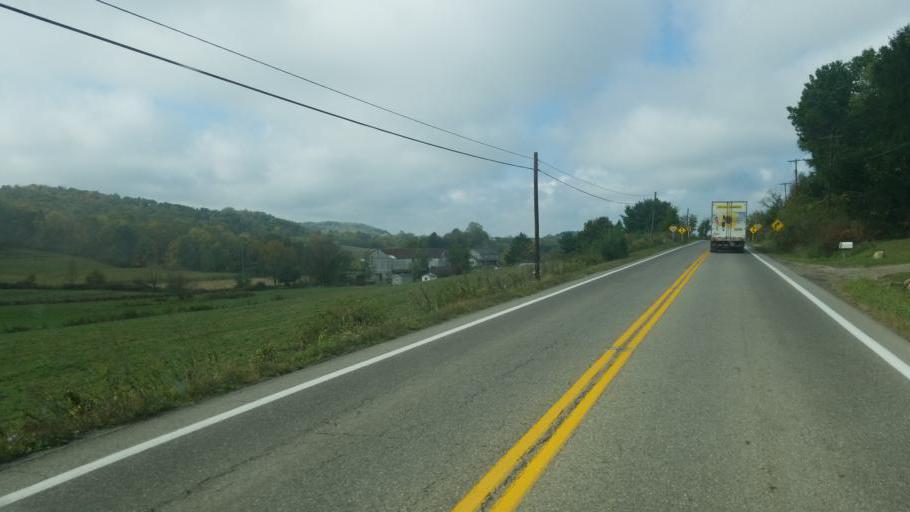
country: US
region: Ohio
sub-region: Stark County
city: Beach City
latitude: 40.6539
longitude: -81.6261
